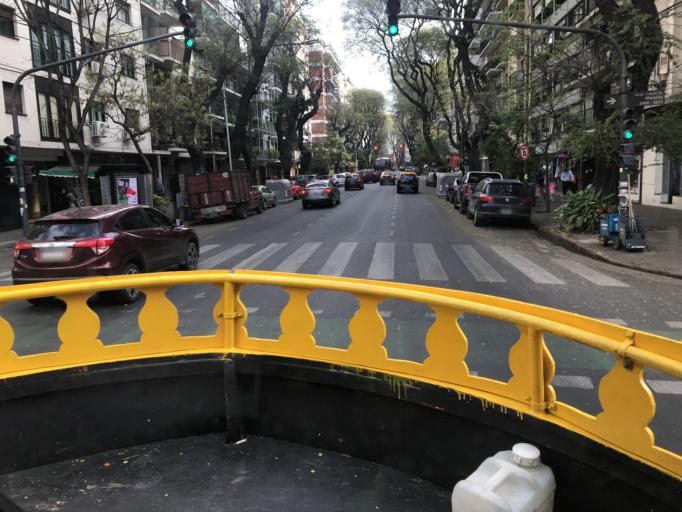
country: AR
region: Buenos Aires F.D.
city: Retiro
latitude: -34.5922
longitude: -58.4128
